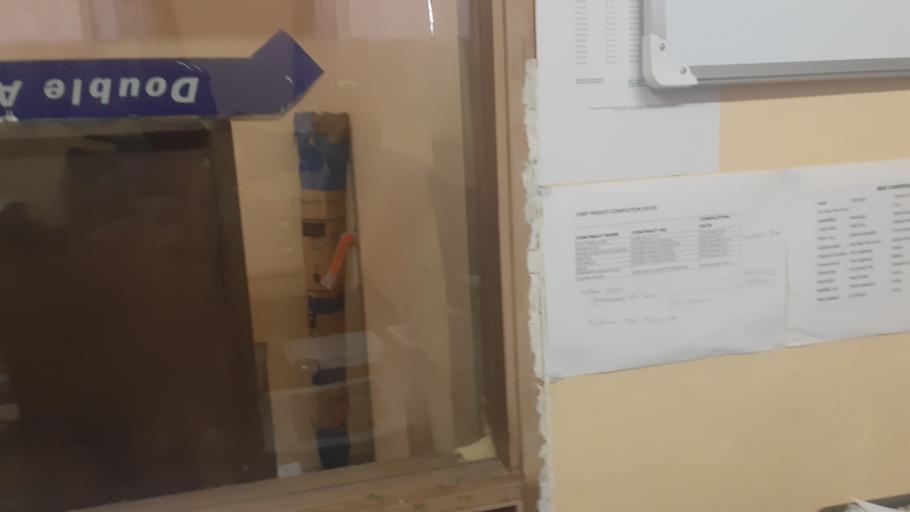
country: VU
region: Shefa
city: Port-Vila
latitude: -17.7195
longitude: 168.3226
